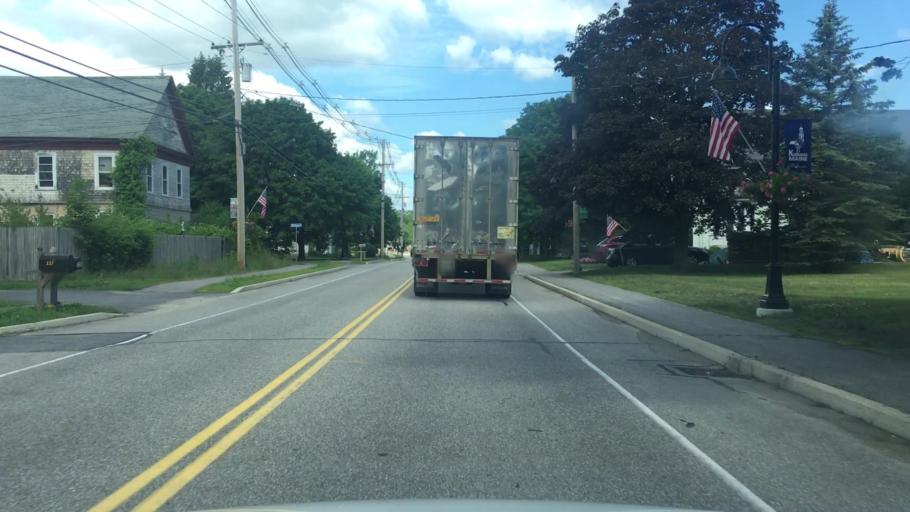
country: US
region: Maine
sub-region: York County
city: West Kennebunk
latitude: 43.4072
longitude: -70.5746
